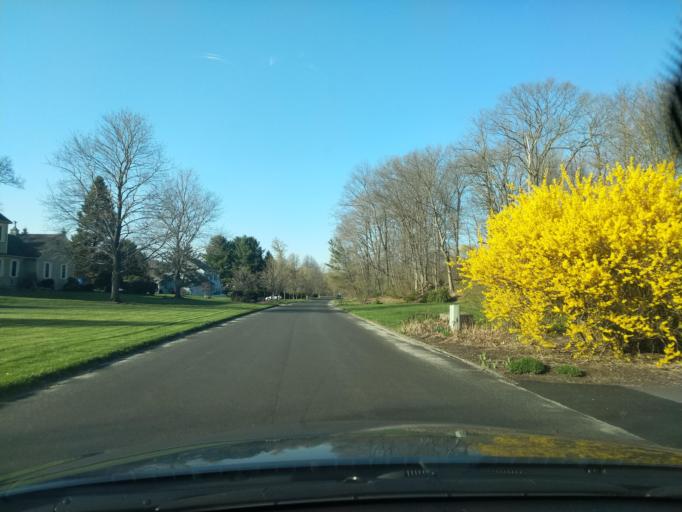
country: US
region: Connecticut
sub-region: Fairfield County
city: Newtown
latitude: 41.3575
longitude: -73.2821
